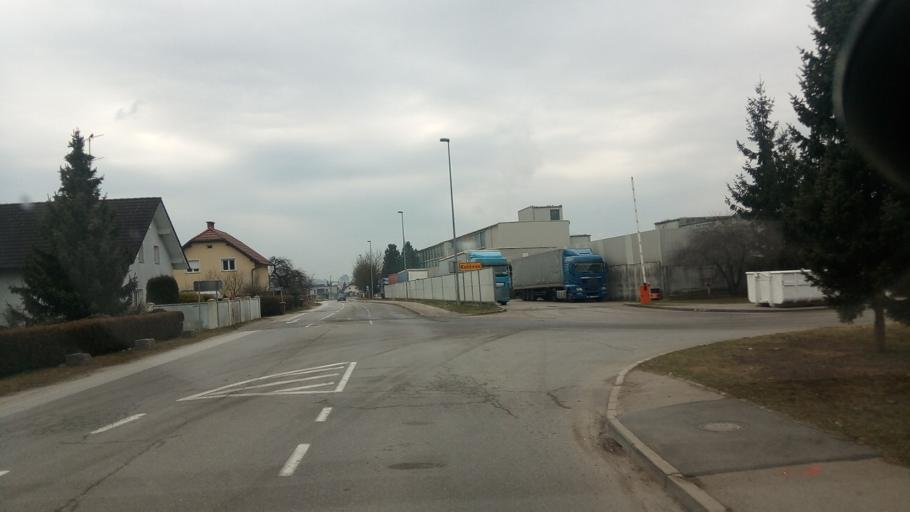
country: SI
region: Domzale
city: Radomlje
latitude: 46.1640
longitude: 14.6086
